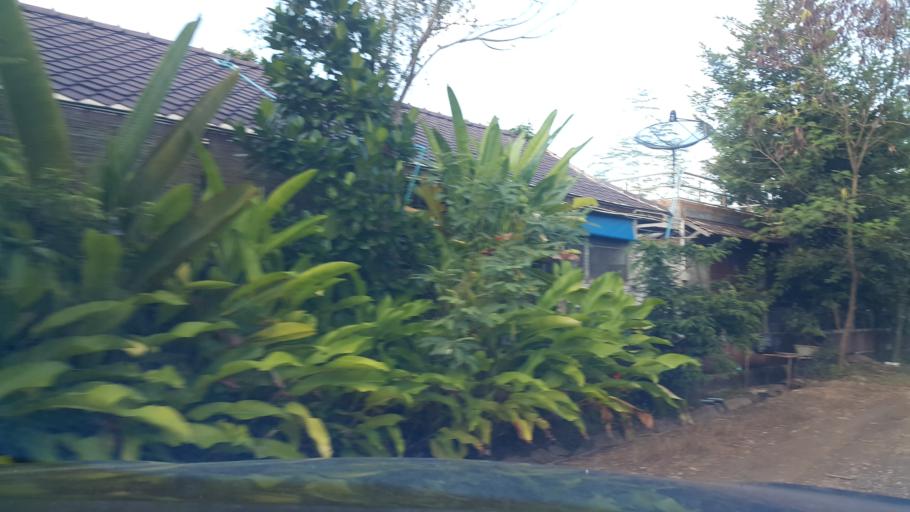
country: TH
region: Chiang Mai
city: Mae Taeng
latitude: 19.1646
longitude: 99.0080
